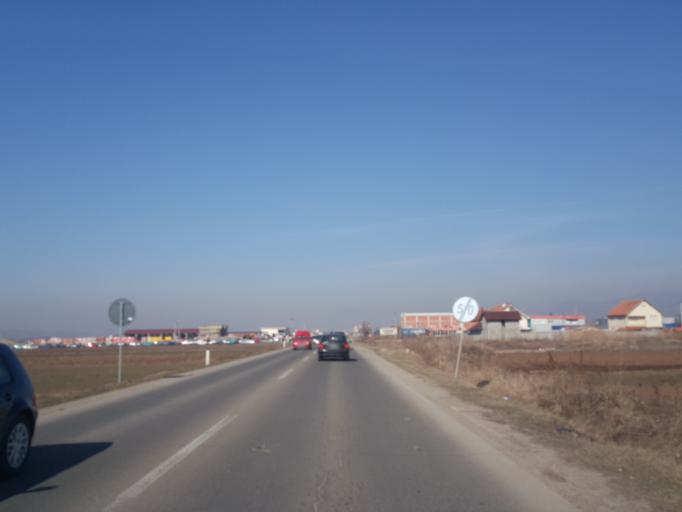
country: XK
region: Mitrovica
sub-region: Vushtrri
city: Vushtrri
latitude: 42.7888
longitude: 21.0063
